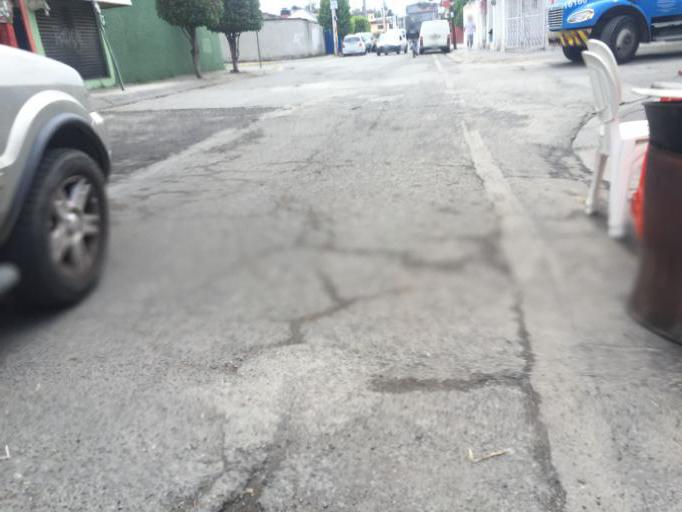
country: MX
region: Mexico
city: Cuautitlan Izcalli
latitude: 19.6582
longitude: -99.2162
